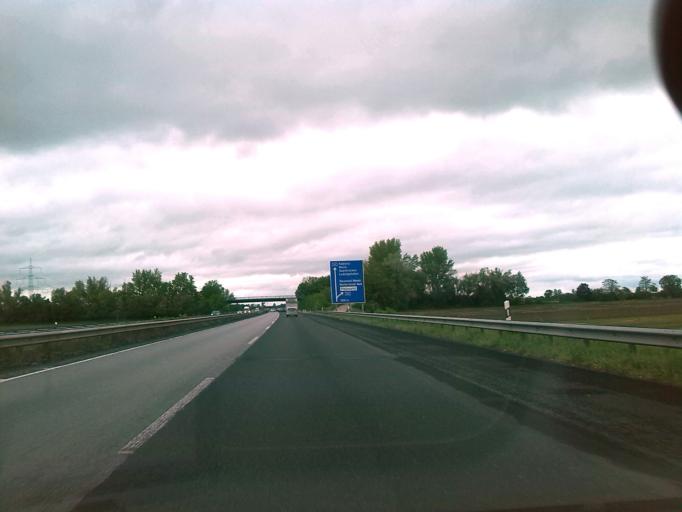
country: DE
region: Rheinland-Pfalz
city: Mutterstadt
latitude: 49.4282
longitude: 8.3346
